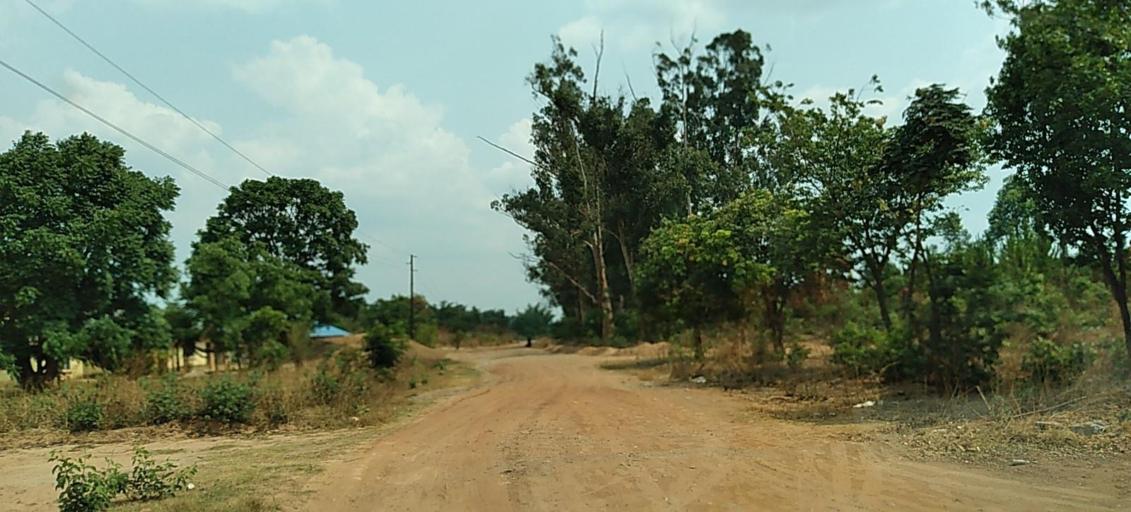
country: ZM
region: Copperbelt
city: Kalulushi
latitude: -12.8264
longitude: 28.0769
